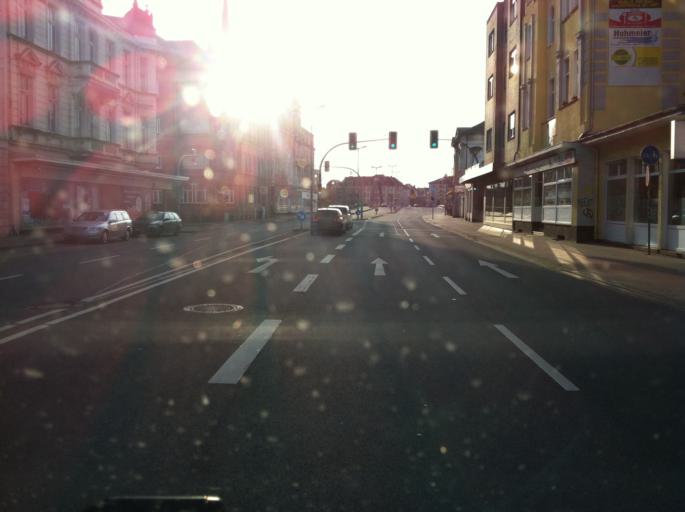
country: DE
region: North Rhine-Westphalia
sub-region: Regierungsbezirk Detmold
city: Minden
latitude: 52.2895
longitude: 8.9275
